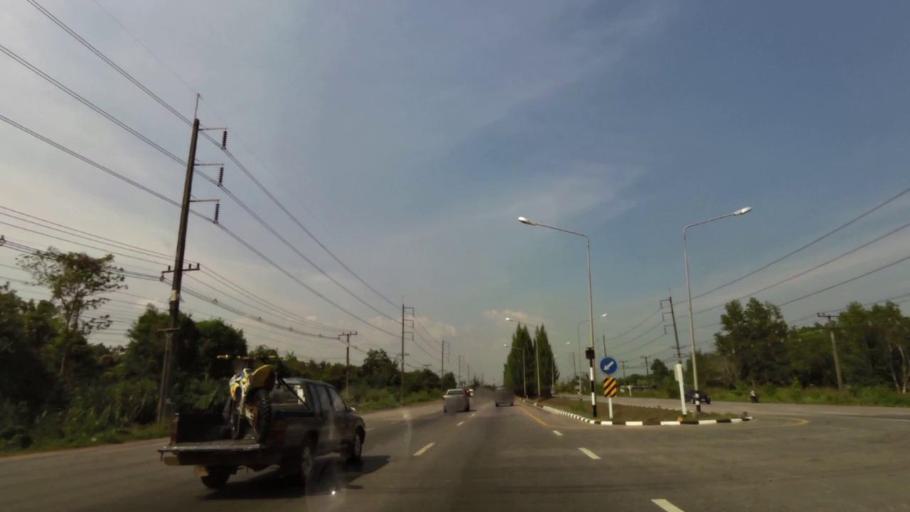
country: TH
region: Chanthaburi
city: Chanthaburi
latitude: 12.6571
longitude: 102.1242
